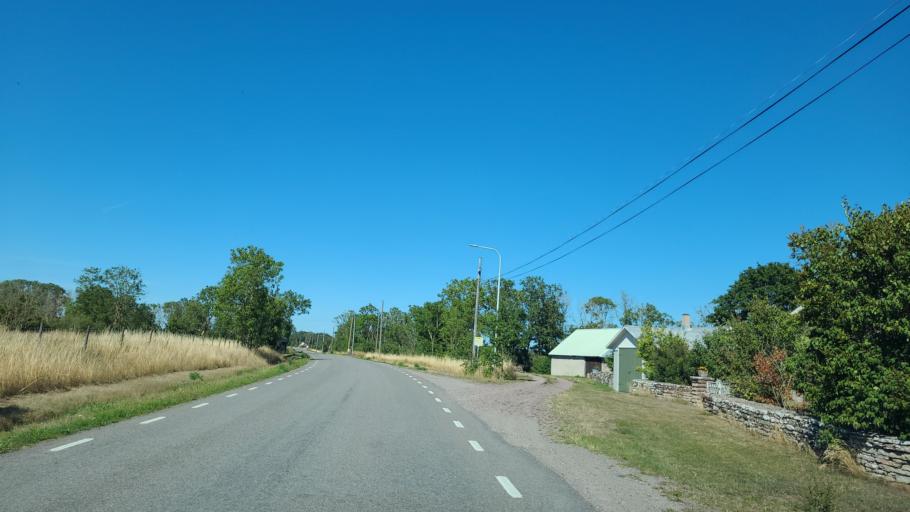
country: SE
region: Kalmar
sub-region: Borgholms Kommun
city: Borgholm
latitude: 56.8988
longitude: 16.8314
